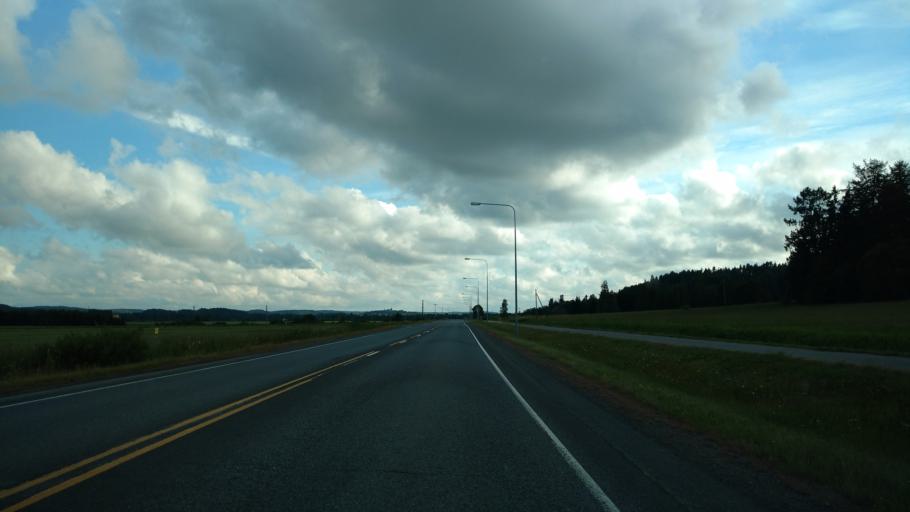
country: FI
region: Varsinais-Suomi
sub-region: Salo
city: Salo
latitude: 60.4142
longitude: 23.1619
